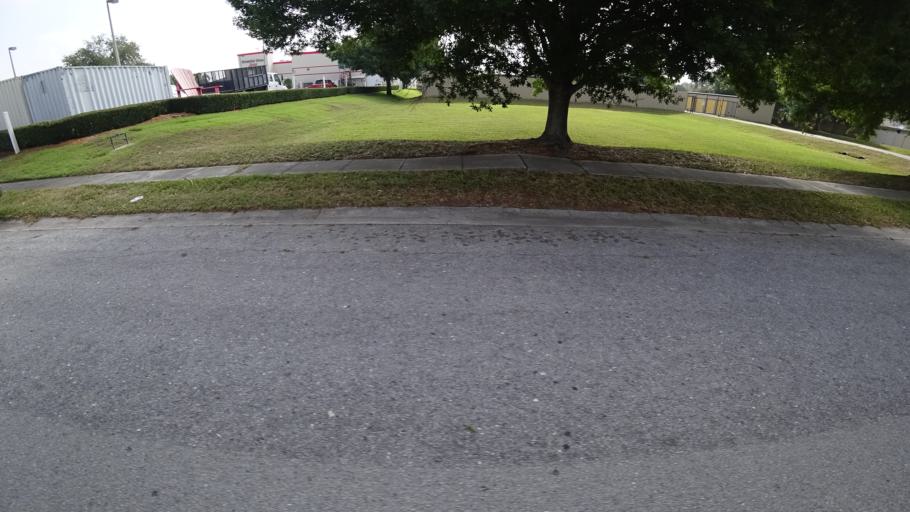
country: US
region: Florida
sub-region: Manatee County
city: West Bradenton
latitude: 27.4946
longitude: -82.6161
